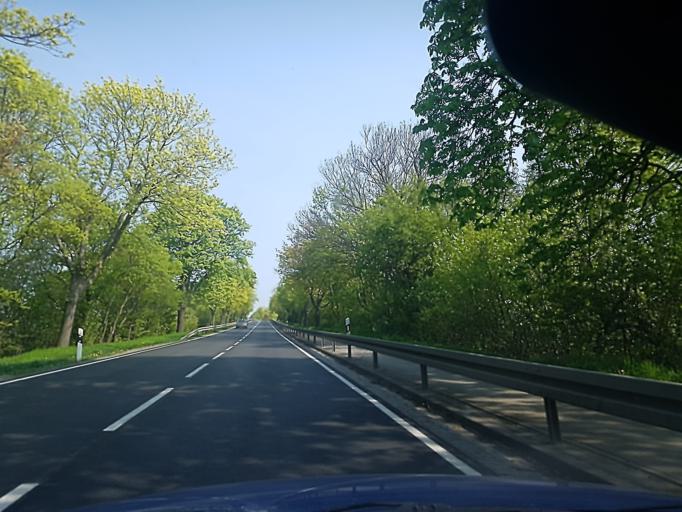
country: DE
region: Saxony
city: Torgau
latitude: 51.5653
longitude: 13.0222
